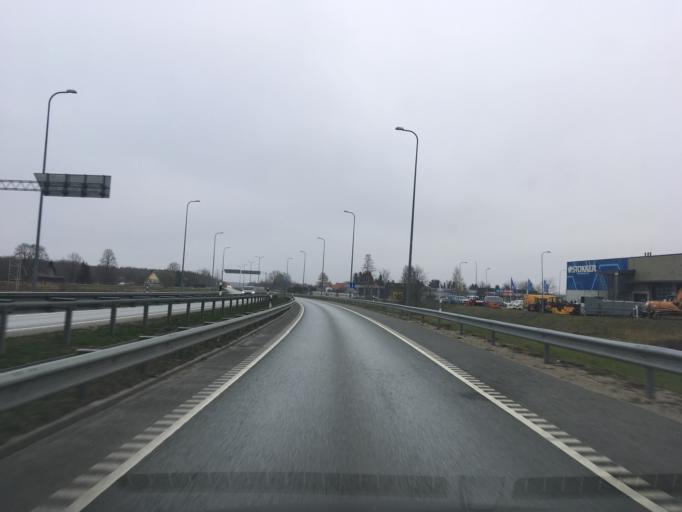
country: EE
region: Ida-Virumaa
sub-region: Johvi vald
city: Johvi
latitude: 59.3685
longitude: 27.3919
